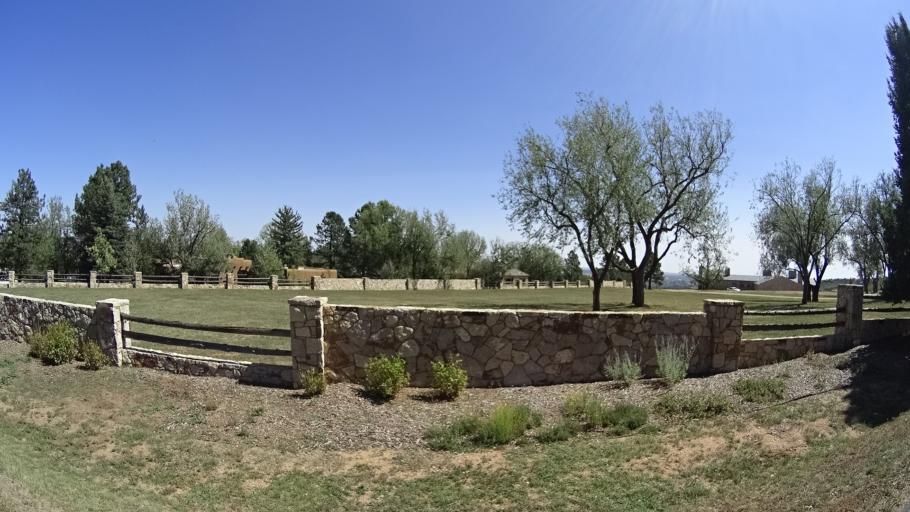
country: US
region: Colorado
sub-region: El Paso County
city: Colorado Springs
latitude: 38.7784
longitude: -104.8424
